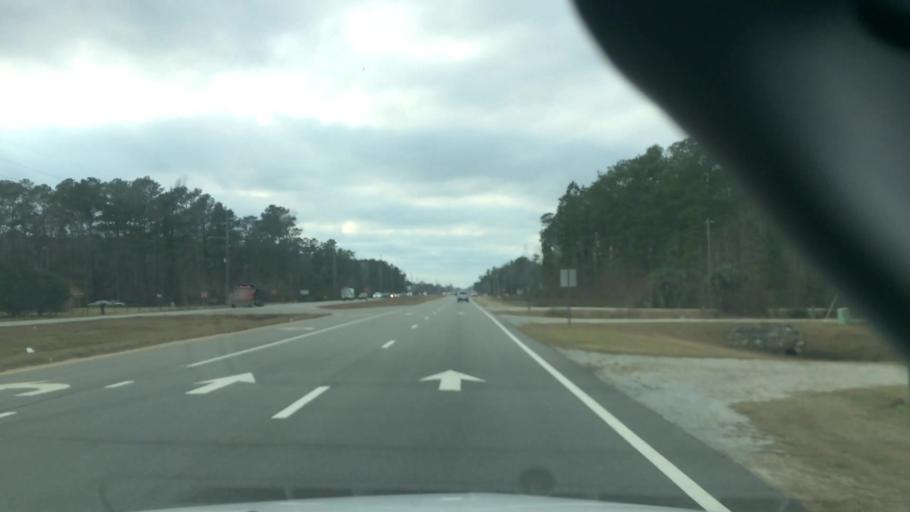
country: US
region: North Carolina
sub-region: Brunswick County
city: Calabash
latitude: 33.9419
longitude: -78.5336
